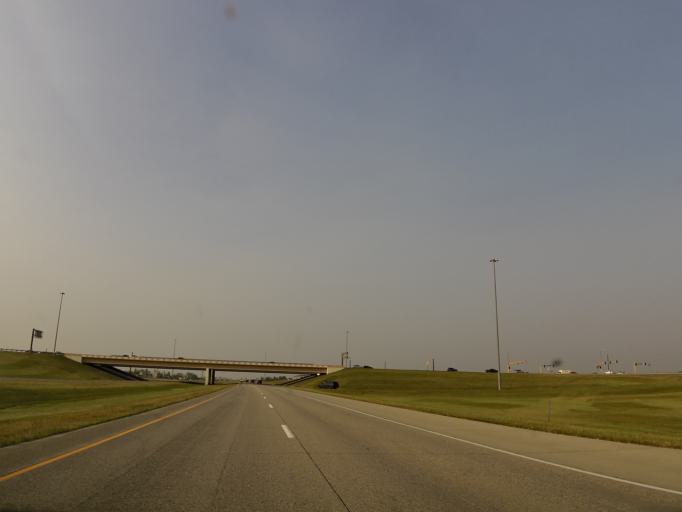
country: US
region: North Dakota
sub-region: Cass County
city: Horace
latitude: 46.8022
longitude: -96.8386
